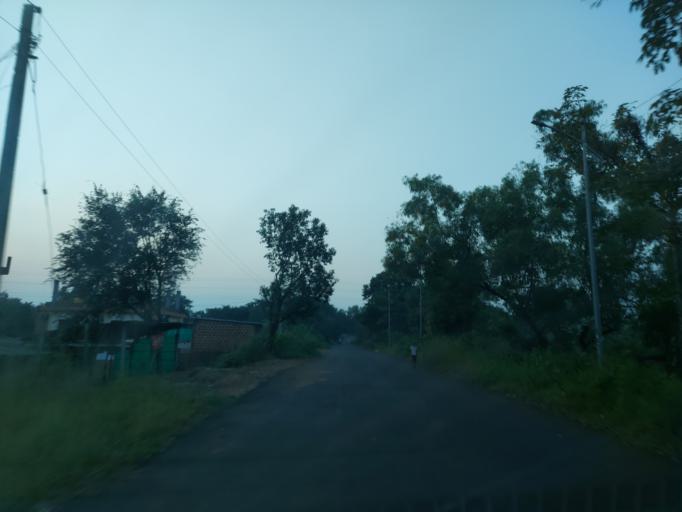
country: IN
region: Maharashtra
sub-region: Sindhudurg
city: Kudal
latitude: 16.1044
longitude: 73.7063
